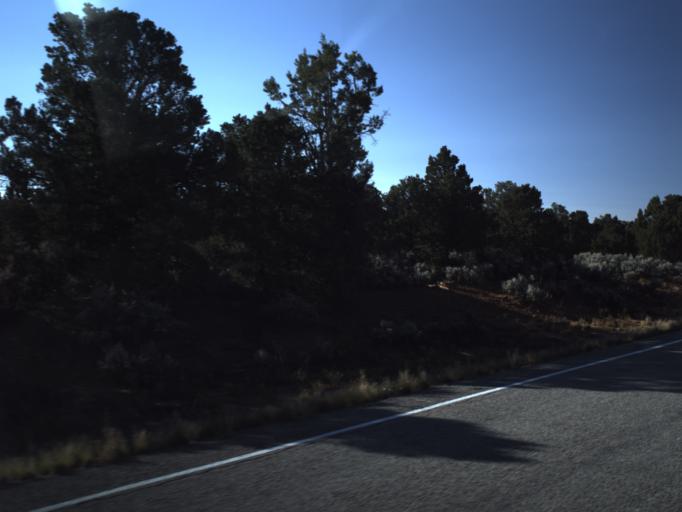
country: US
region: Utah
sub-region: San Juan County
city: Blanding
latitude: 37.5761
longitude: -109.9201
